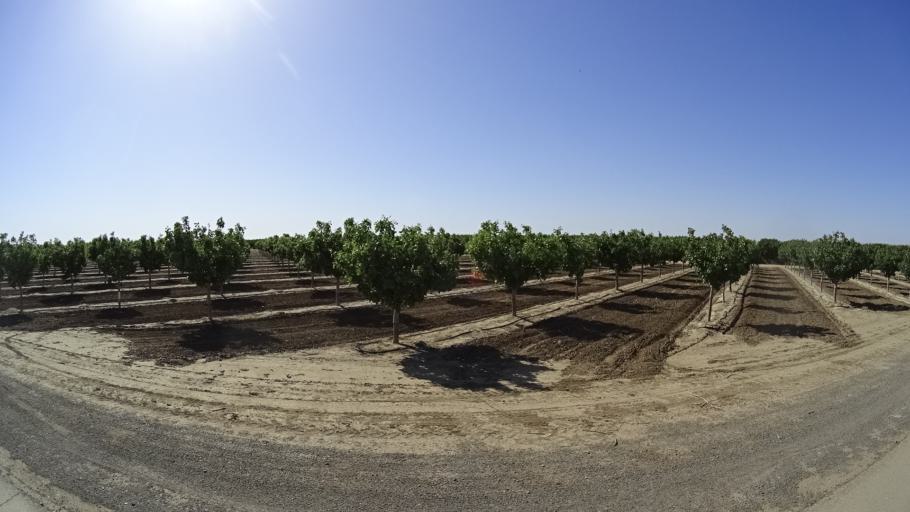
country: US
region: California
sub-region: Fresno County
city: Huron
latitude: 36.1239
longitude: -120.0291
